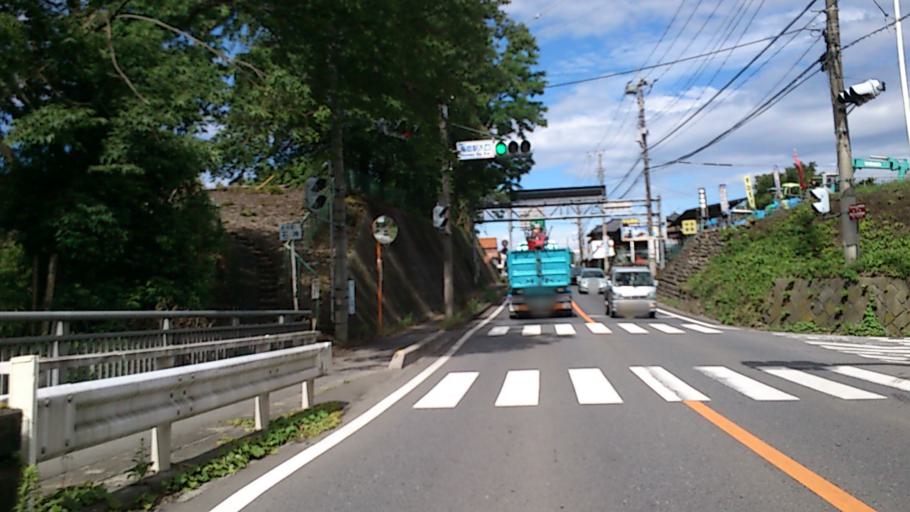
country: JP
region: Gunma
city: Yoshii
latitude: 36.2547
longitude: 139.0092
